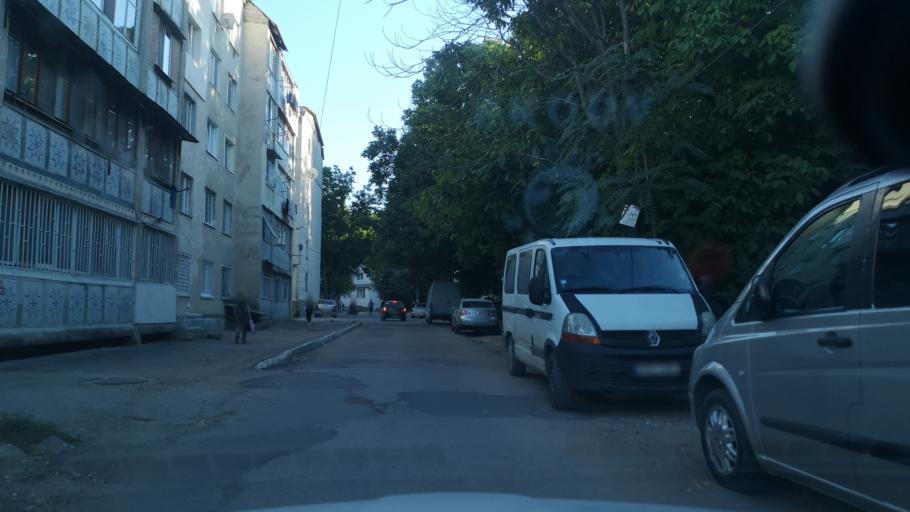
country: MD
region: Chisinau
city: Chisinau
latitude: 46.9883
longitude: 28.8752
